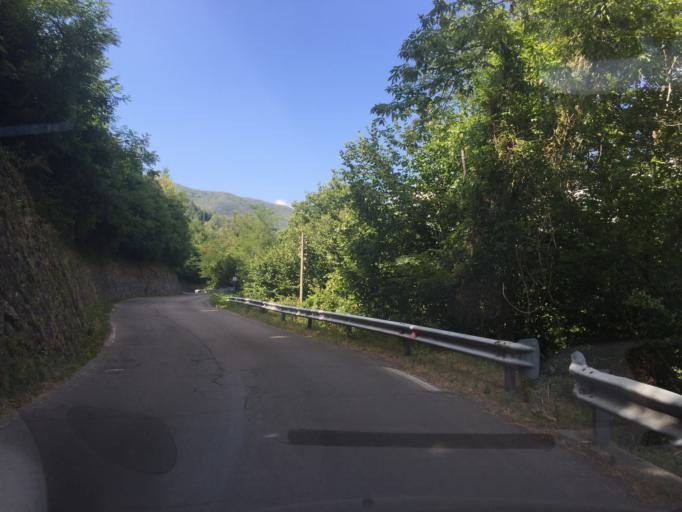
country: IT
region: Tuscany
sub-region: Provincia di Lucca
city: Fontana delle Monache
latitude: 44.1204
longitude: 10.3016
